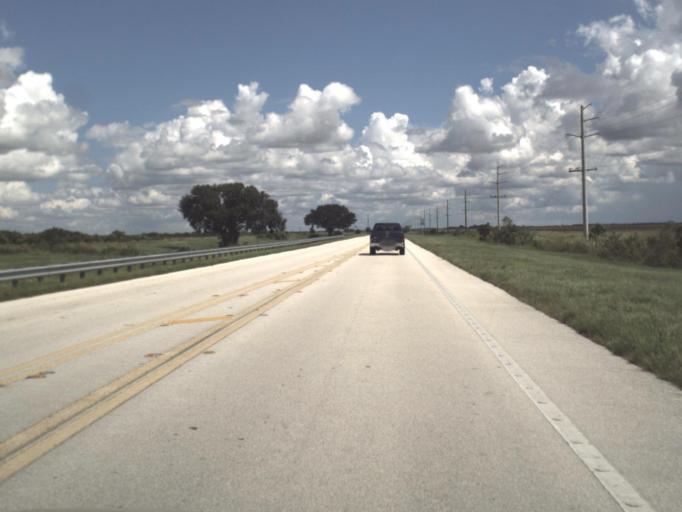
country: US
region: Florida
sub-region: Highlands County
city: Placid Lakes
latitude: 27.2096
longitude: -81.5941
